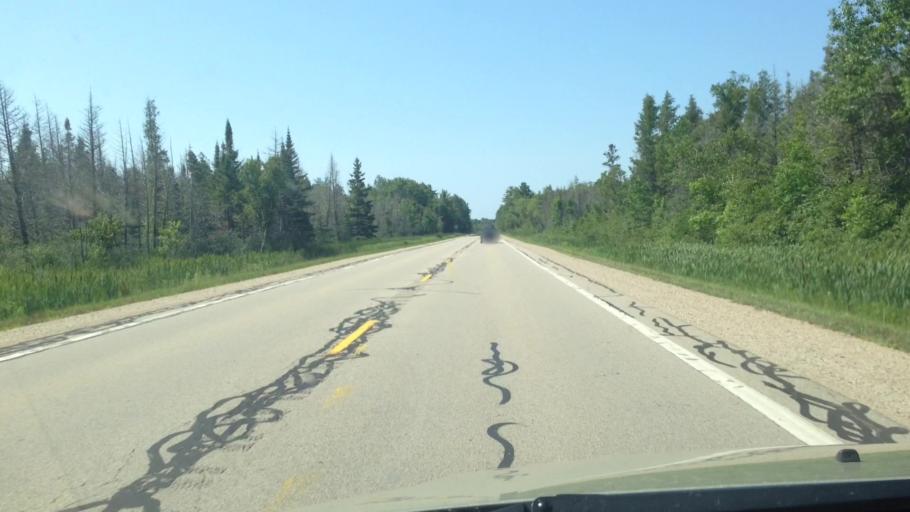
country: US
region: Michigan
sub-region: Menominee County
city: Menominee
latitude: 45.3930
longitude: -87.3690
